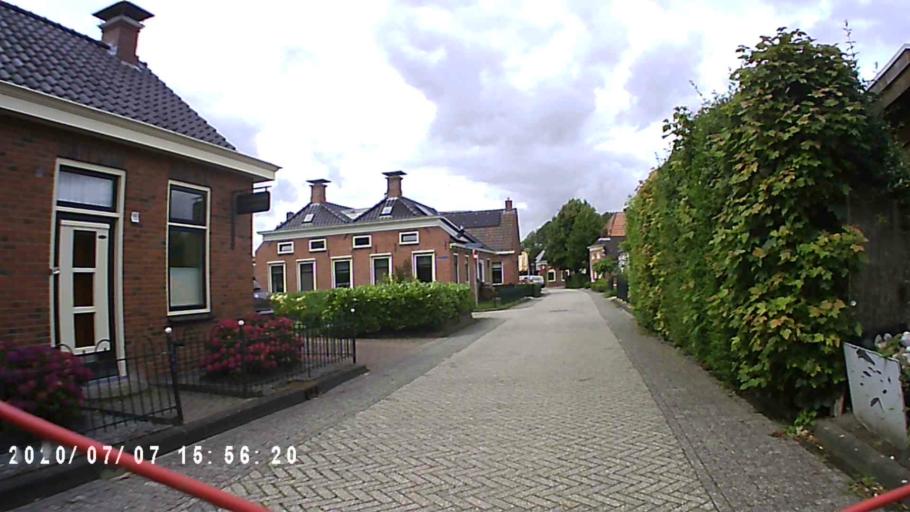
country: NL
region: Groningen
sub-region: Gemeente Winsum
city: Winsum
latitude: 53.3629
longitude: 6.5146
